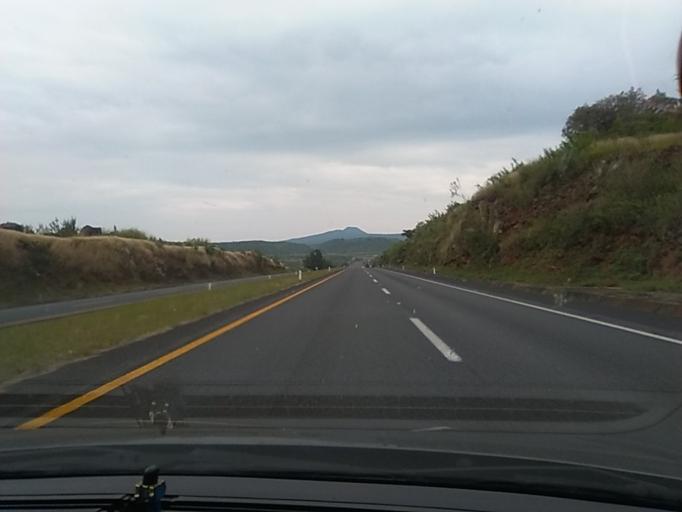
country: MX
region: Michoacan
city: Penjamillo de Degollado
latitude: 20.0504
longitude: -101.9544
